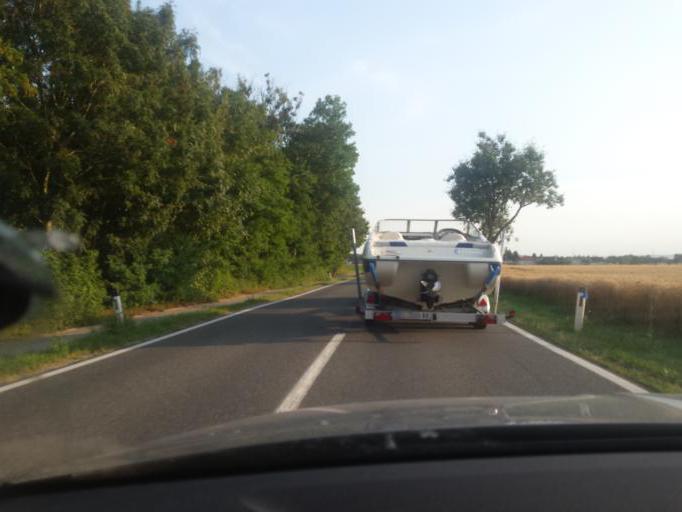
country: AT
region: Lower Austria
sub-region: Politischer Bezirk Bruck an der Leitha
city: Rohrau
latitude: 48.0536
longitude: 16.8419
